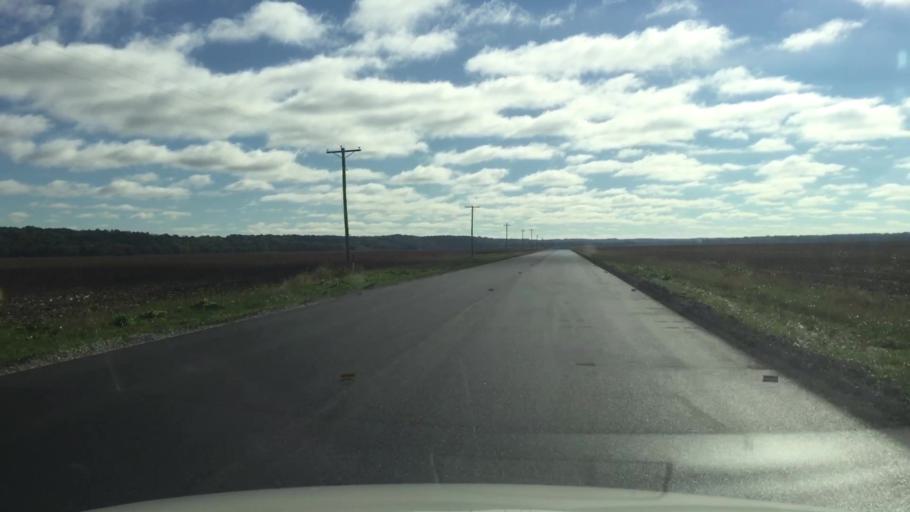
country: US
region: Missouri
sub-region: Howard County
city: New Franklin
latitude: 38.9957
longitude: -92.6619
